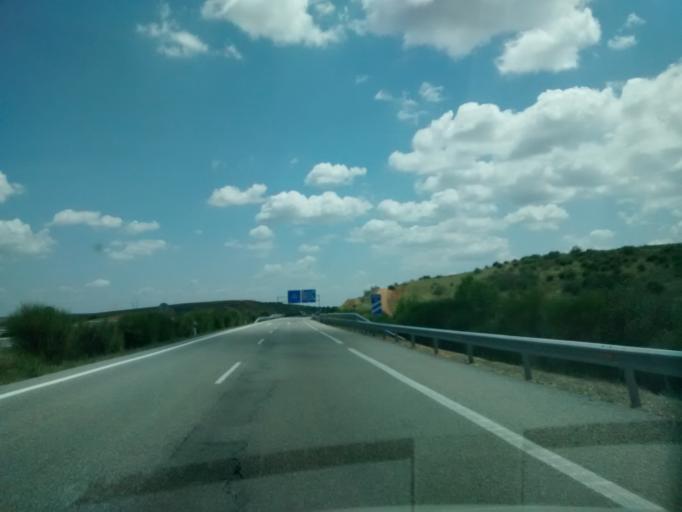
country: ES
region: Castille and Leon
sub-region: Provincia de Leon
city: Astorga
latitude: 42.4388
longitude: -6.0603
